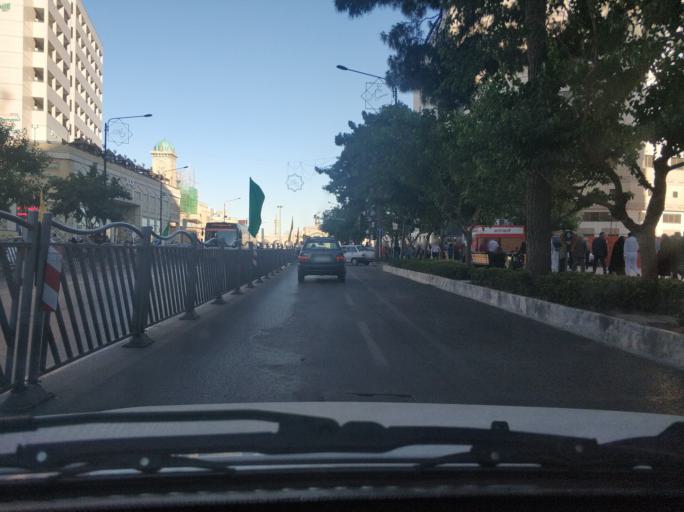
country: IR
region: Razavi Khorasan
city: Mashhad
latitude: 36.2923
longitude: 59.6119
